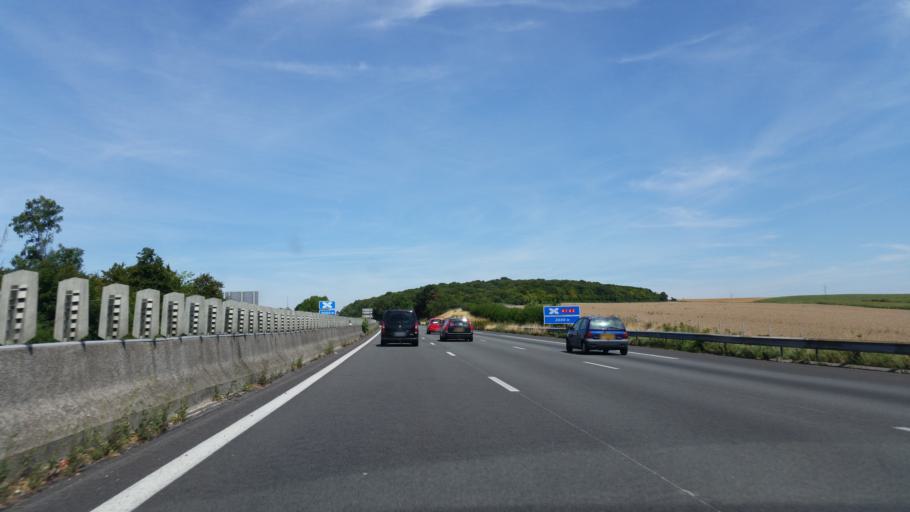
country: FR
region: Picardie
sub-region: Departement de la Somme
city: Peronne
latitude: 49.9899
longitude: 2.8727
